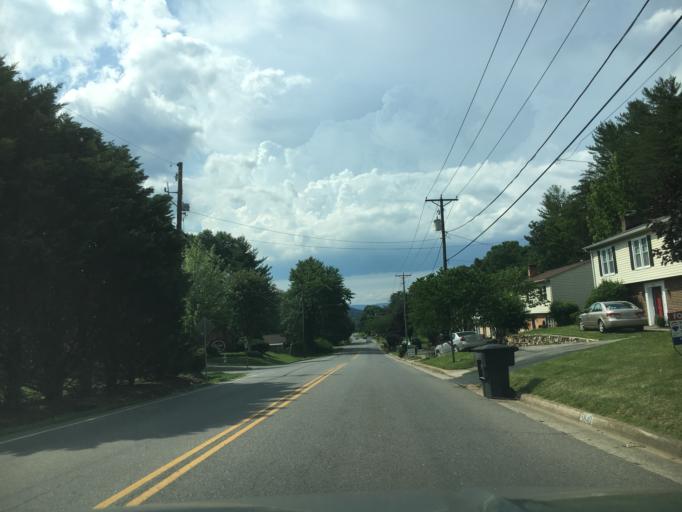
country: US
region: Virginia
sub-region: Roanoke County
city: Cave Spring
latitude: 37.2084
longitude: -80.0100
